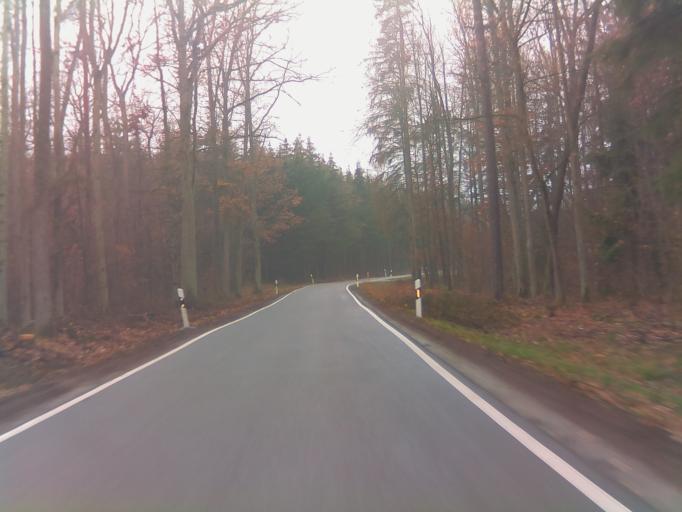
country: DE
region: Bavaria
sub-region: Regierungsbezirk Unterfranken
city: Hochheim
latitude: 50.4020
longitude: 10.4575
